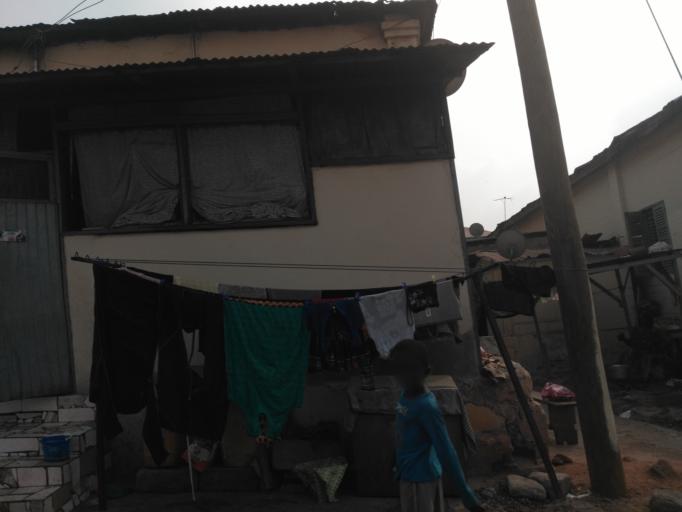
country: GH
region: Ashanti
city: Kumasi
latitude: 6.6903
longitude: -1.6166
